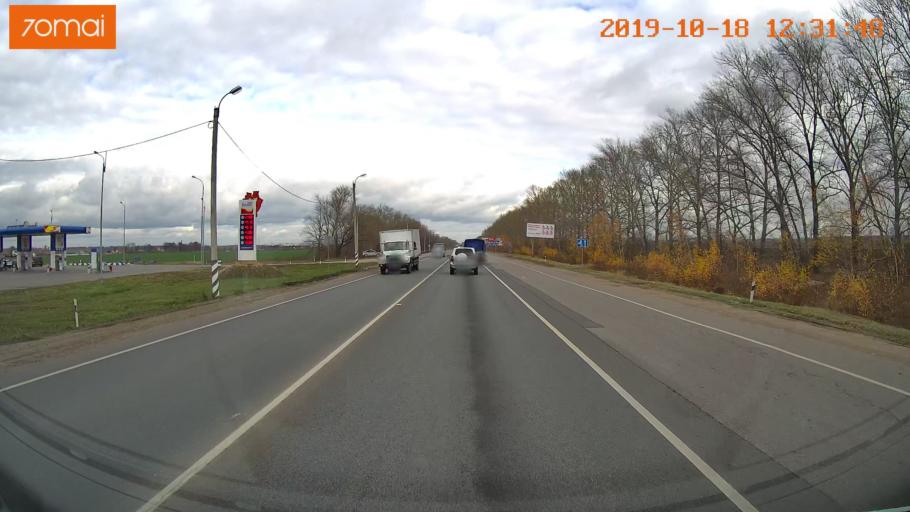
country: RU
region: Rjazan
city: Ryazan'
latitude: 54.5960
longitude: 39.6170
